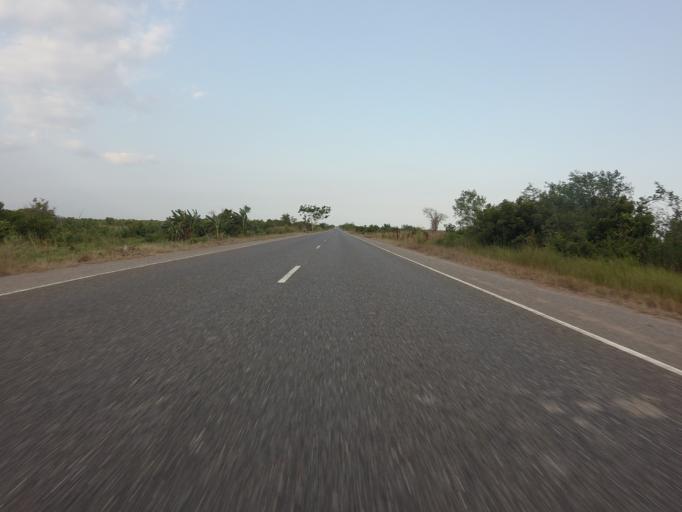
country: GH
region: Volta
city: Anloga
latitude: 6.0833
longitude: 0.5639
